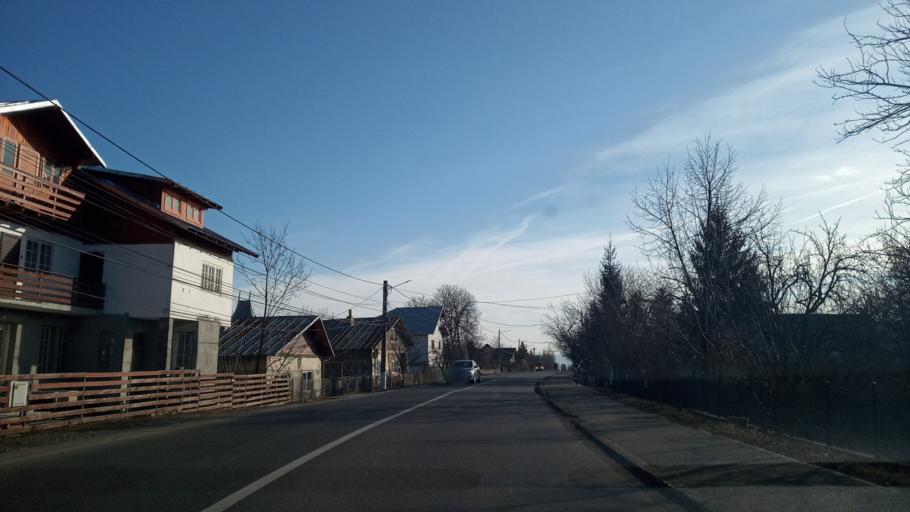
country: RO
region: Prahova
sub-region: Oras Breaza
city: Breaza de Jos
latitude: 45.1665
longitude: 25.6822
